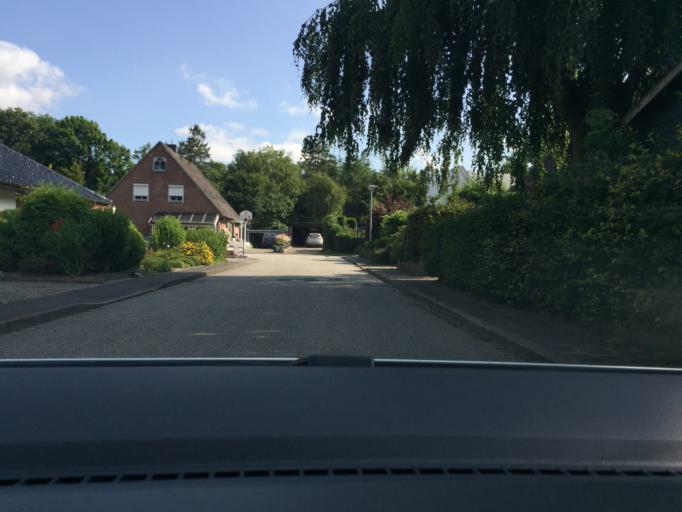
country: DE
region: Schleswig-Holstein
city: Itzehoe
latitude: 53.9415
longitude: 9.5321
